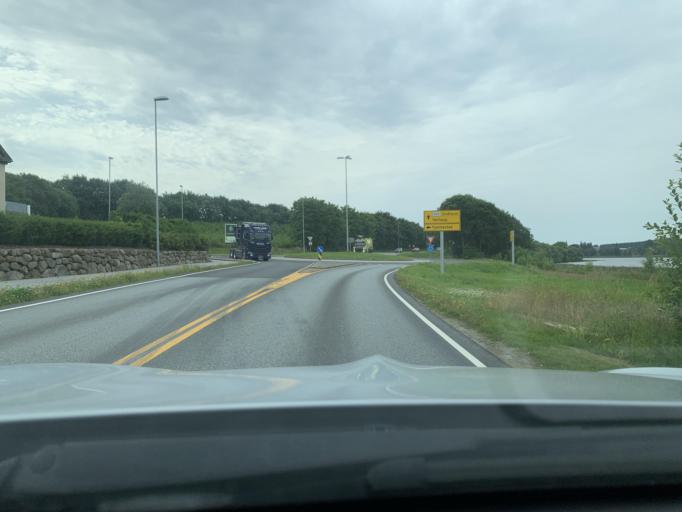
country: NO
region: Rogaland
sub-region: Sandnes
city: Sandnes
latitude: 58.7717
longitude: 5.7250
